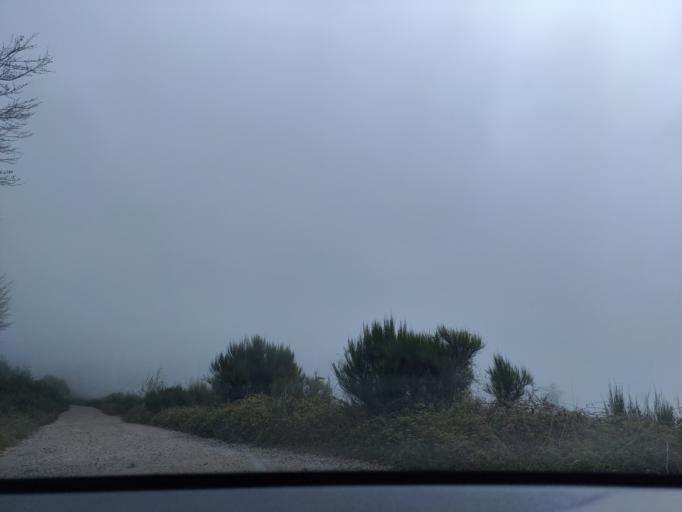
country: ES
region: Catalonia
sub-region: Provincia de Barcelona
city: Fogars de Montclus
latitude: 41.7582
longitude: 2.4538
